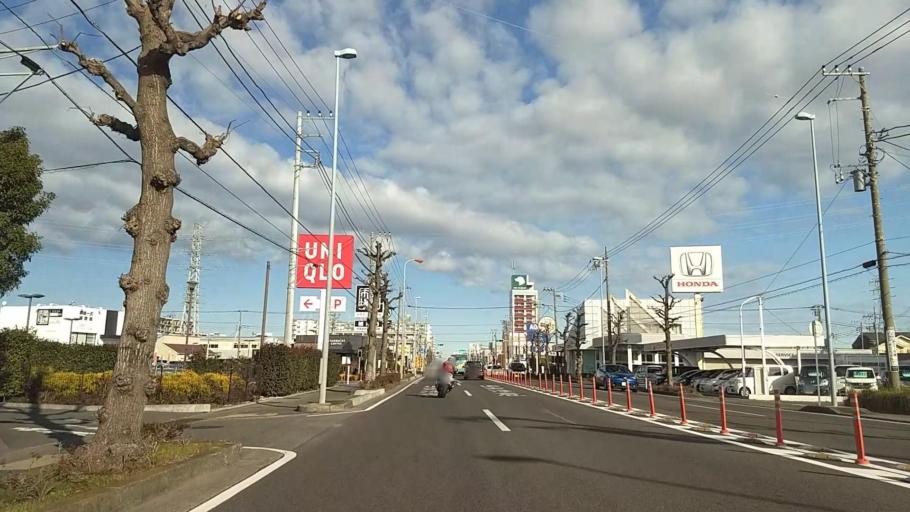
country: JP
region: Kanagawa
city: Hiratsuka
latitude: 35.3652
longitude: 139.3615
